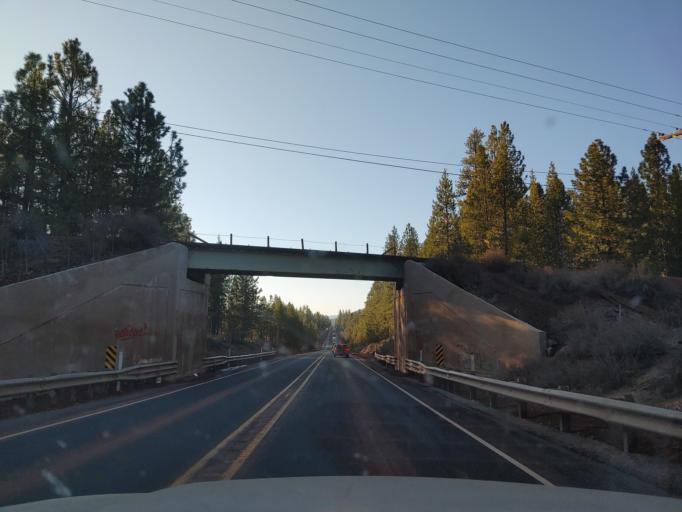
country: US
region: Oregon
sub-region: Deschutes County
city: La Pine
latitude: 43.3768
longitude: -121.7975
